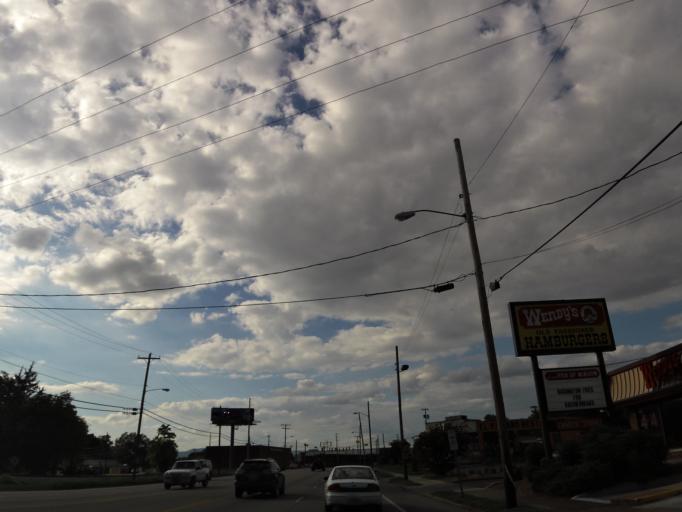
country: US
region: Georgia
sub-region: Walker County
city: Rossville
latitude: 34.9883
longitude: -85.2889
